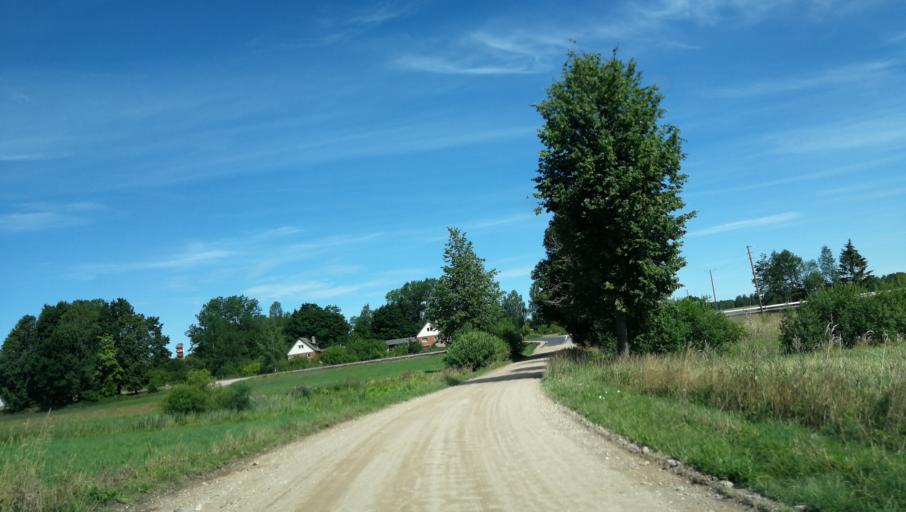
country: LV
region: Gulbenes Rajons
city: Gulbene
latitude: 57.1846
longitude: 26.8618
